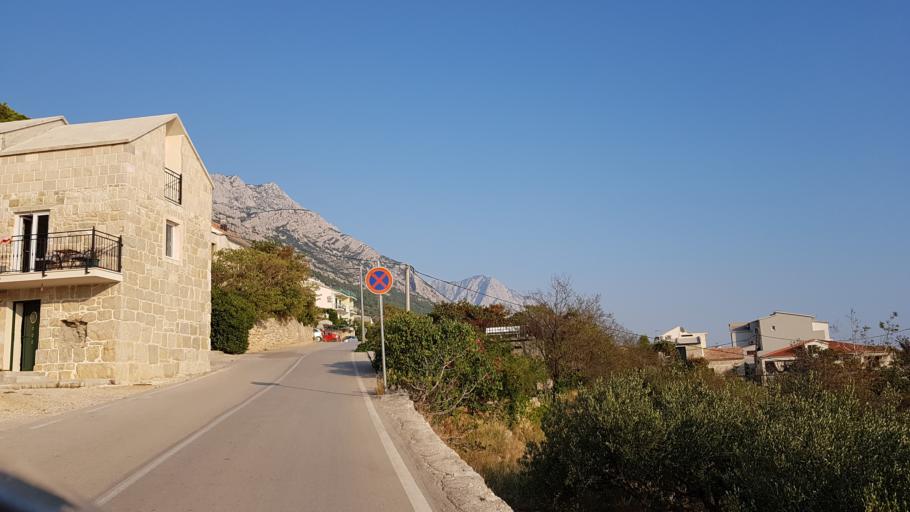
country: HR
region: Splitsko-Dalmatinska
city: Donja Brela
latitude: 43.3837
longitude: 16.9094
